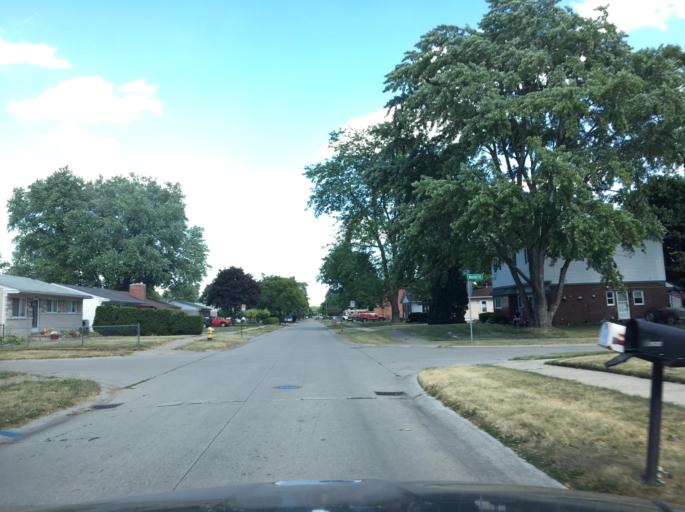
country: US
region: Michigan
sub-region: Macomb County
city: Fraser
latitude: 42.5419
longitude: -82.9137
